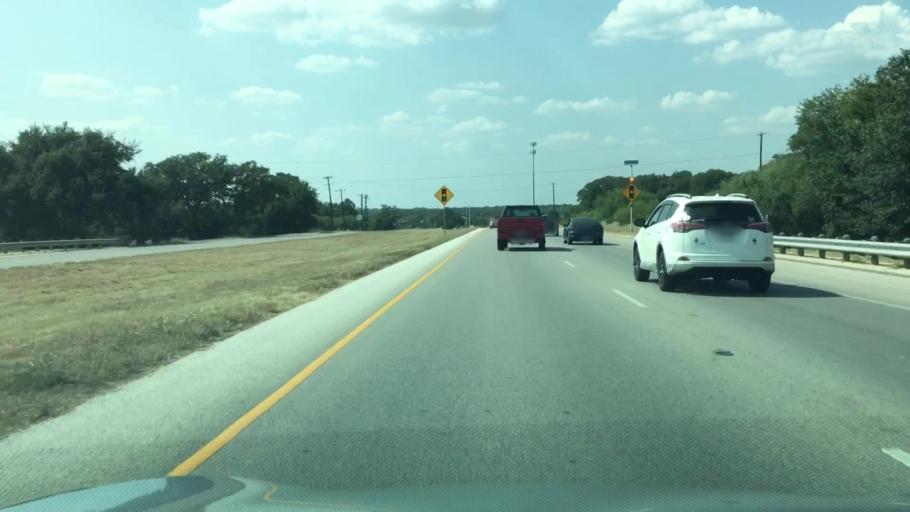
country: US
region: Texas
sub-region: Hays County
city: San Marcos
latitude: 29.8774
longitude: -97.9690
